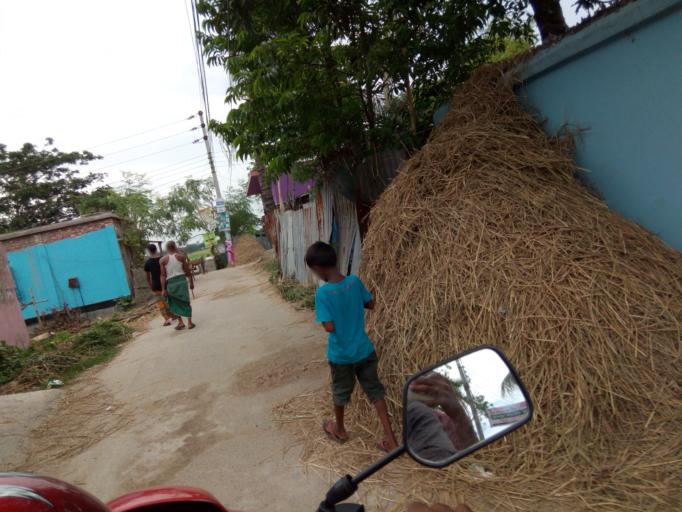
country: BD
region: Dhaka
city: Paltan
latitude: 23.7454
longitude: 90.4872
